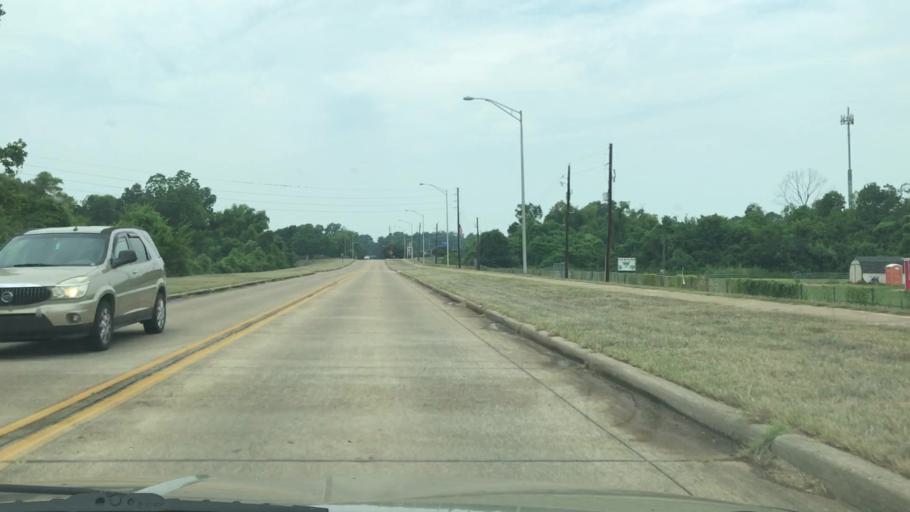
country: US
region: Louisiana
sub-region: Bossier Parish
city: Bossier City
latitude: 32.4708
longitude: -93.7029
